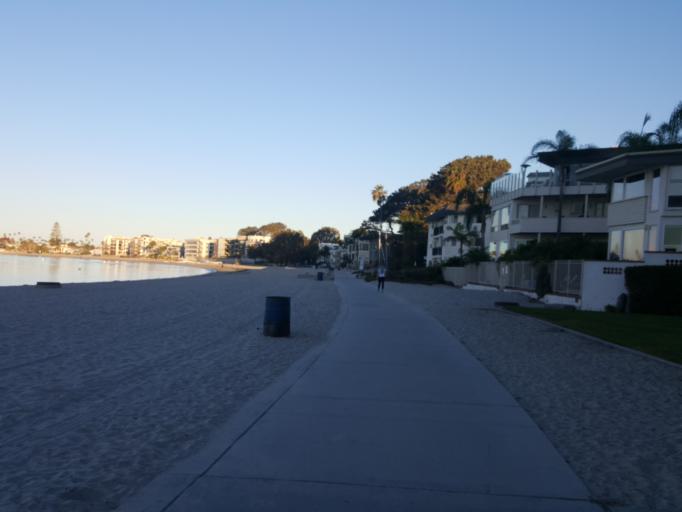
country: US
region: California
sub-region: San Diego County
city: La Jolla
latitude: 32.7898
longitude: -117.2416
